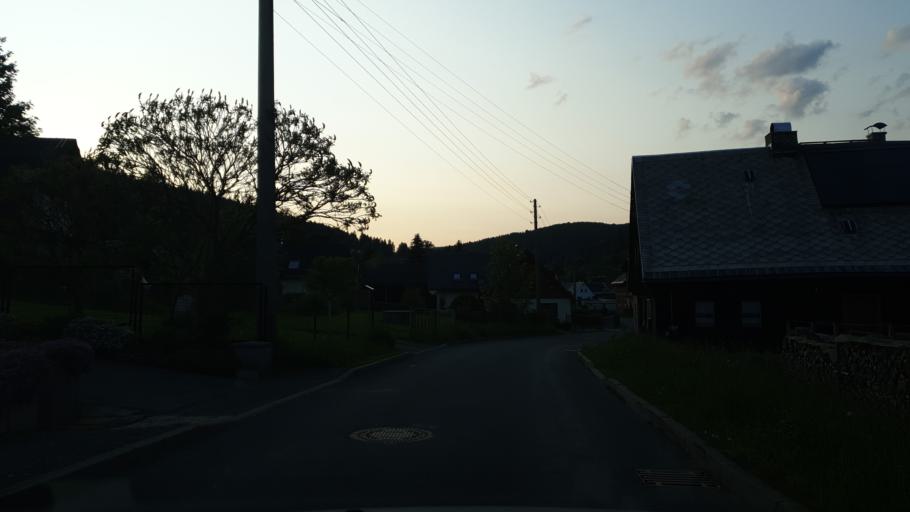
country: DE
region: Saxony
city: Klingenthal
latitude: 50.3745
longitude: 12.4660
